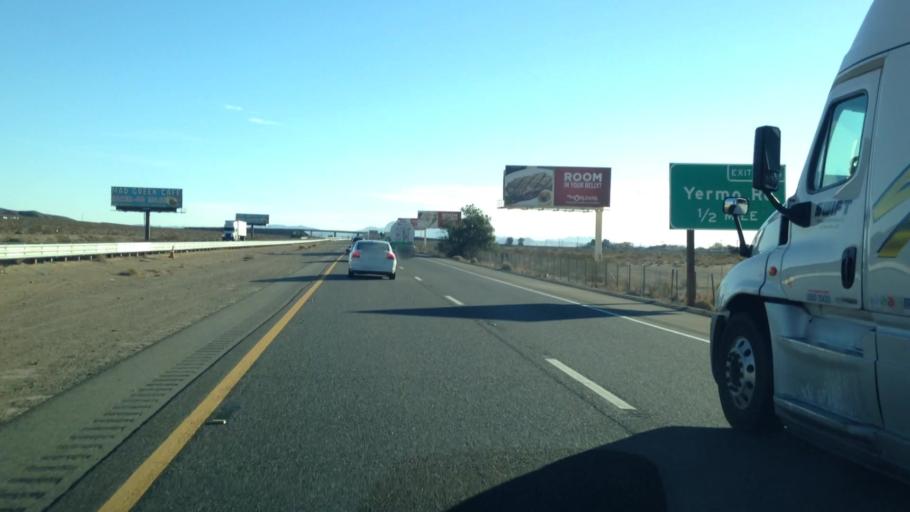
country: US
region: California
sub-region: San Bernardino County
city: Barstow
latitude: 34.9110
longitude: -116.8195
